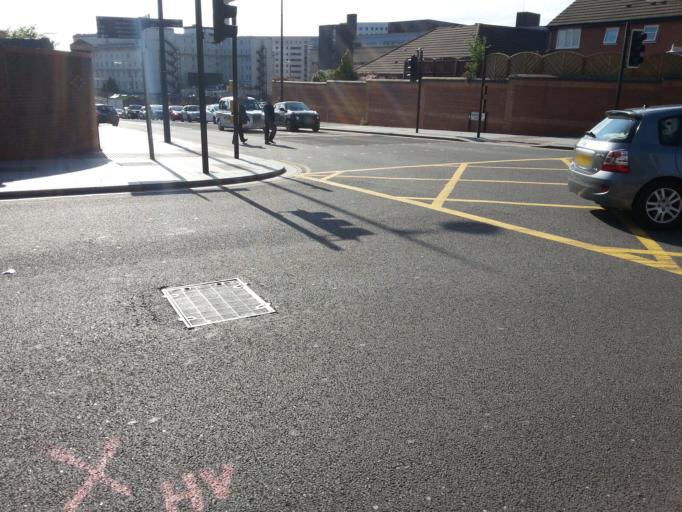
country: GB
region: England
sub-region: Liverpool
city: Liverpool
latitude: 53.4054
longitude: -2.9729
